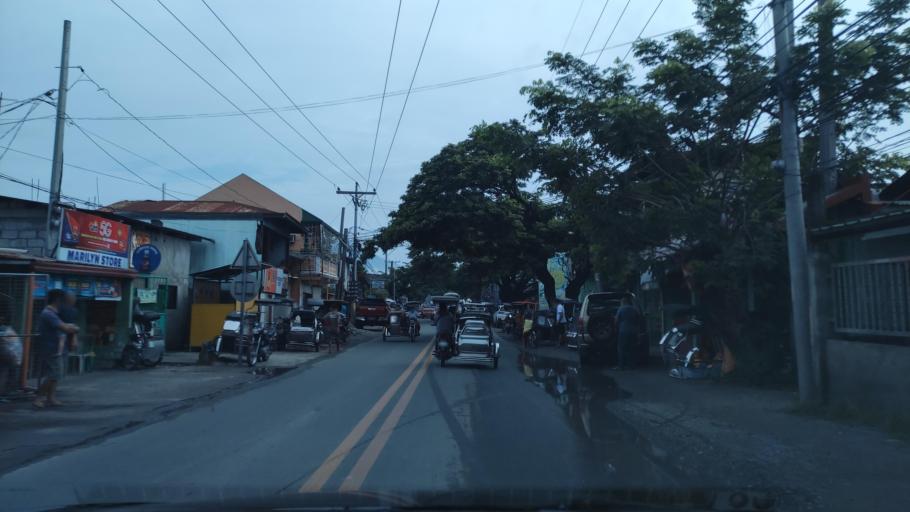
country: PH
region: Central Luzon
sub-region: Province of Pampanga
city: Arayat
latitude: 15.1272
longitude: 120.7757
